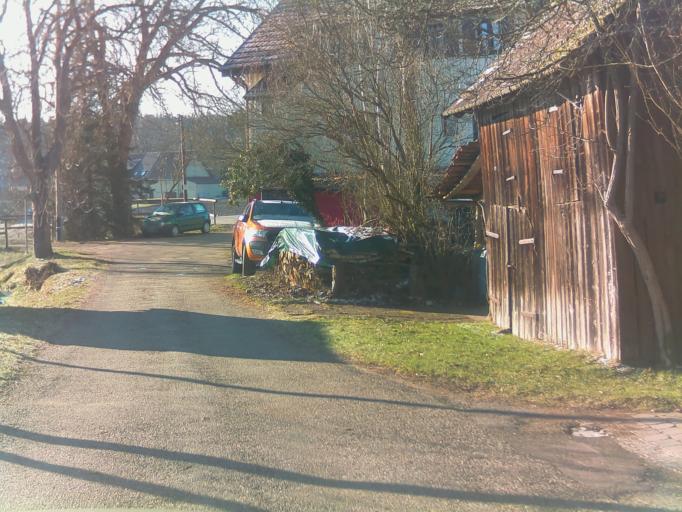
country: DE
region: Baden-Wuerttemberg
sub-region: Karlsruhe Region
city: Oberreichenbach
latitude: 48.7360
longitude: 8.6582
